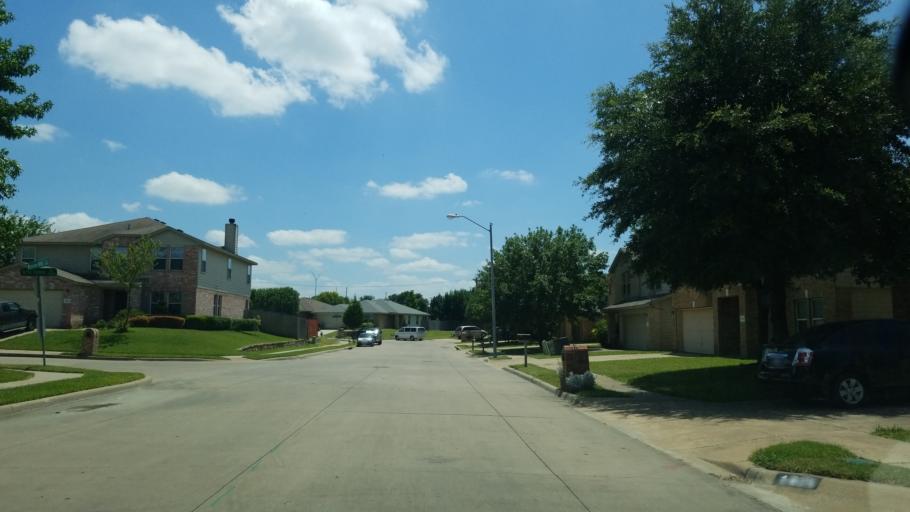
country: US
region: Texas
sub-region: Dallas County
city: Hutchins
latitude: 32.7368
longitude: -96.7136
